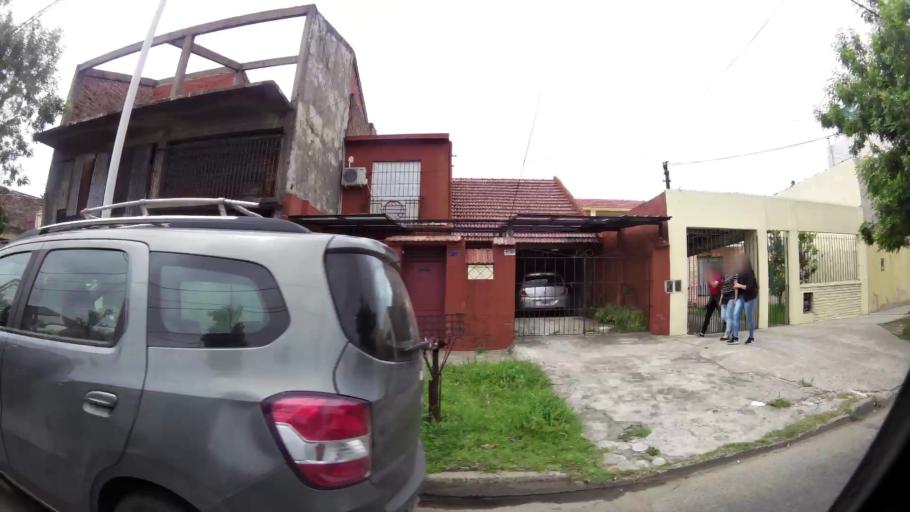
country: AR
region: Buenos Aires
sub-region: Partido de Avellaneda
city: Avellaneda
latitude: -34.6778
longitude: -58.3732
